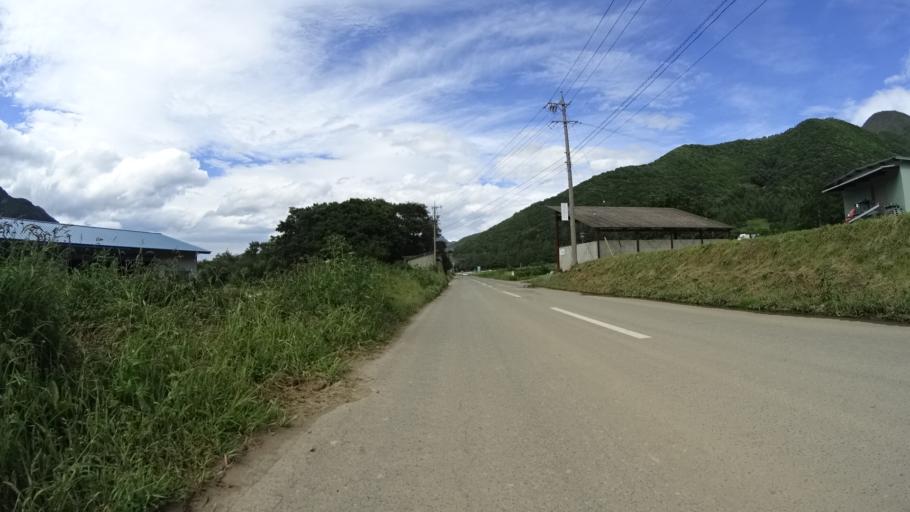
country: JP
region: Yamanashi
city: Nirasaki
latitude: 35.9348
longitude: 138.5458
